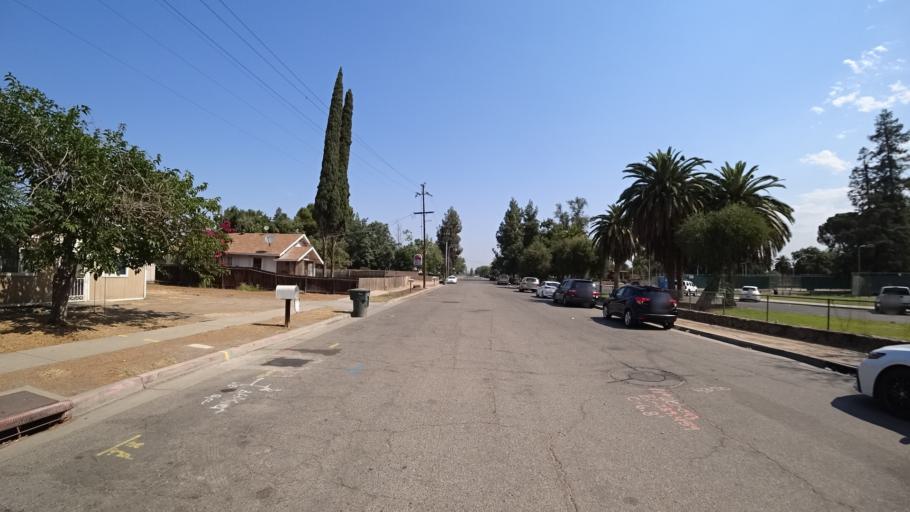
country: US
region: California
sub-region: Fresno County
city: West Park
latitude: 36.7560
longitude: -119.8267
